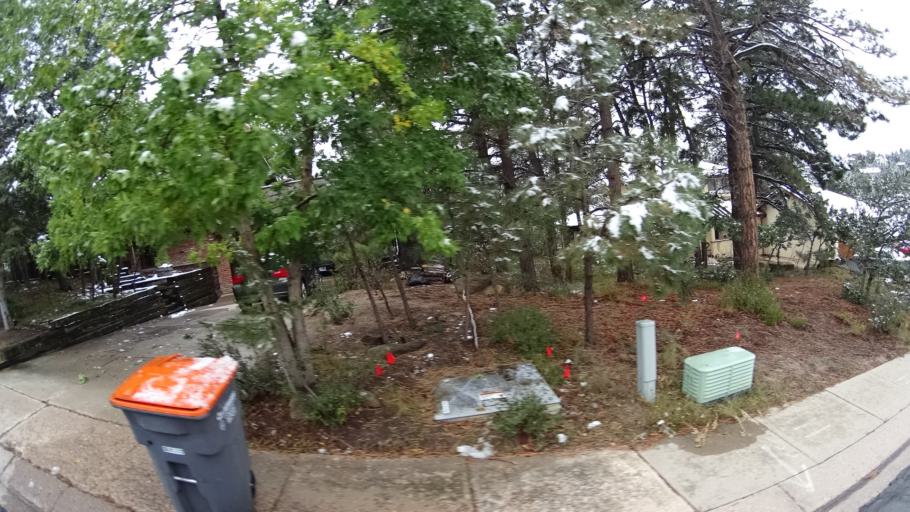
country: US
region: Colorado
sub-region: El Paso County
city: Colorado Springs
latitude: 38.9158
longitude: -104.7980
